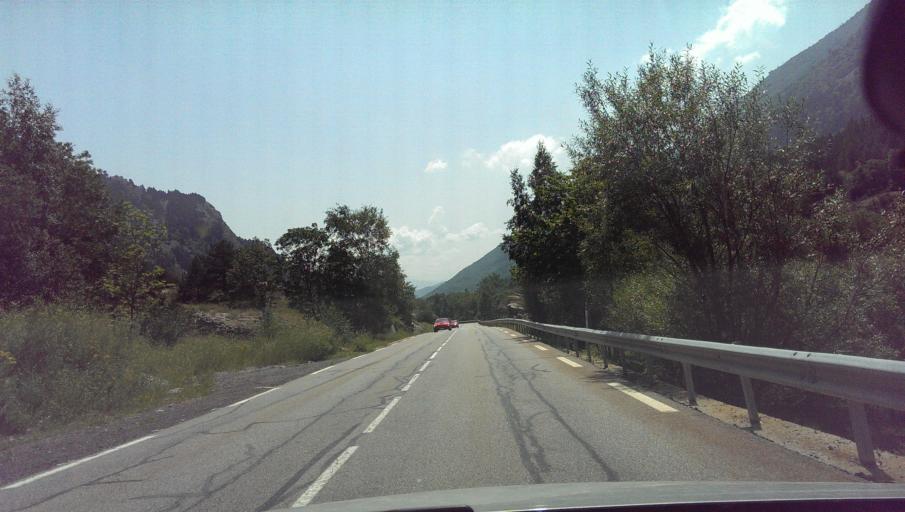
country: ES
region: Catalonia
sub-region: Provincia de Girona
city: Meranges
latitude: 42.5121
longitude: 1.8273
